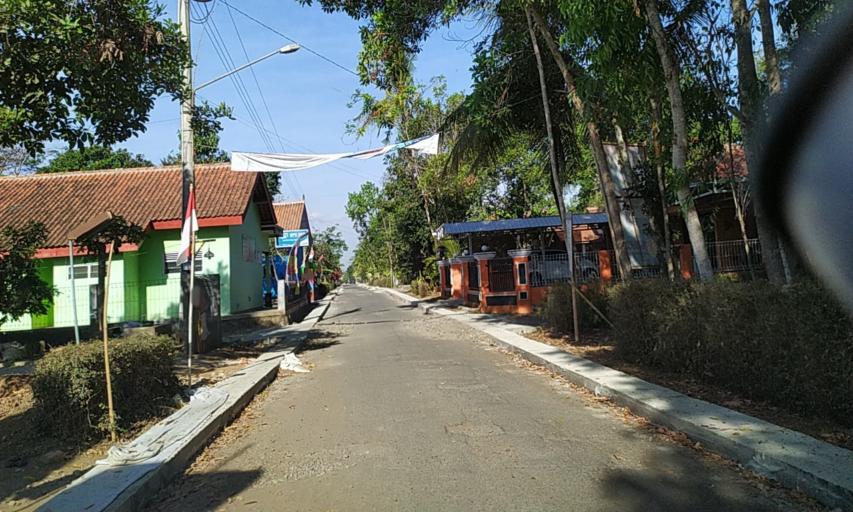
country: ID
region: Central Java
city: Rawaseser
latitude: -7.6148
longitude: 109.2663
